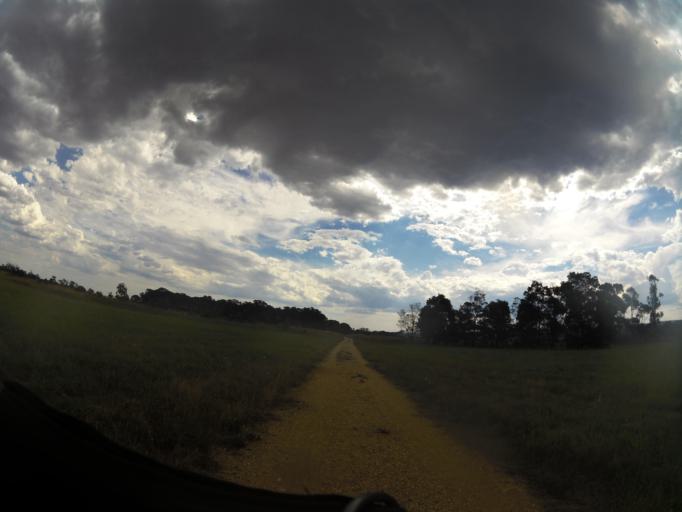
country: AU
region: Victoria
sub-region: Wellington
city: Heyfield
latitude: -38.0156
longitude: 146.6903
